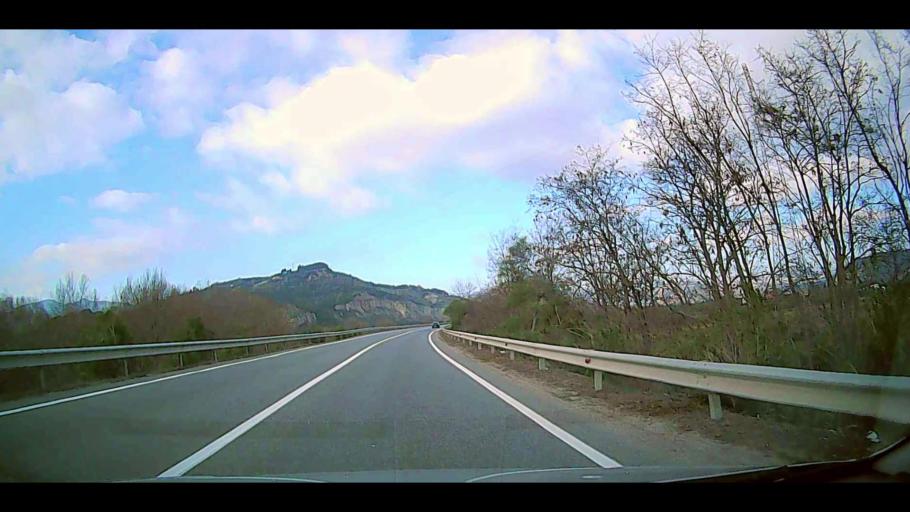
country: IT
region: Calabria
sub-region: Provincia di Crotone
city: Scandale
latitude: 39.1656
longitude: 16.9554
